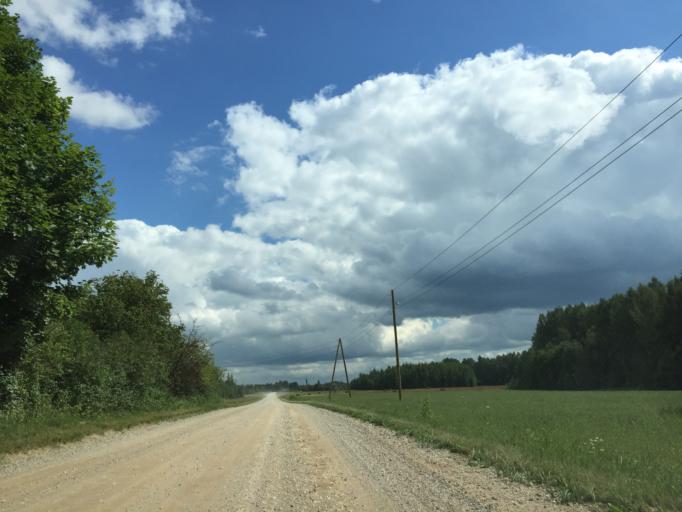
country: LV
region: Malpils
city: Malpils
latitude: 56.8718
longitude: 25.0055
